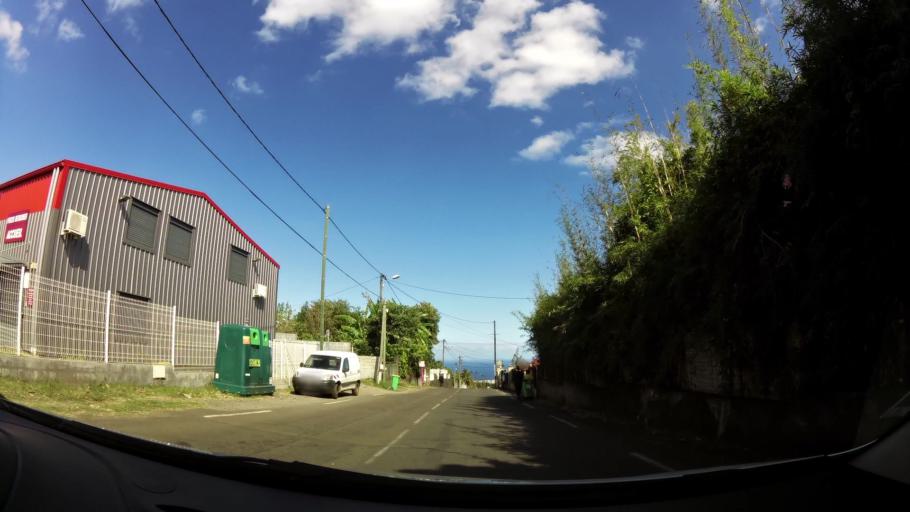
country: RE
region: Reunion
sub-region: Reunion
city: Le Tampon
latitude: -21.2871
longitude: 55.5099
